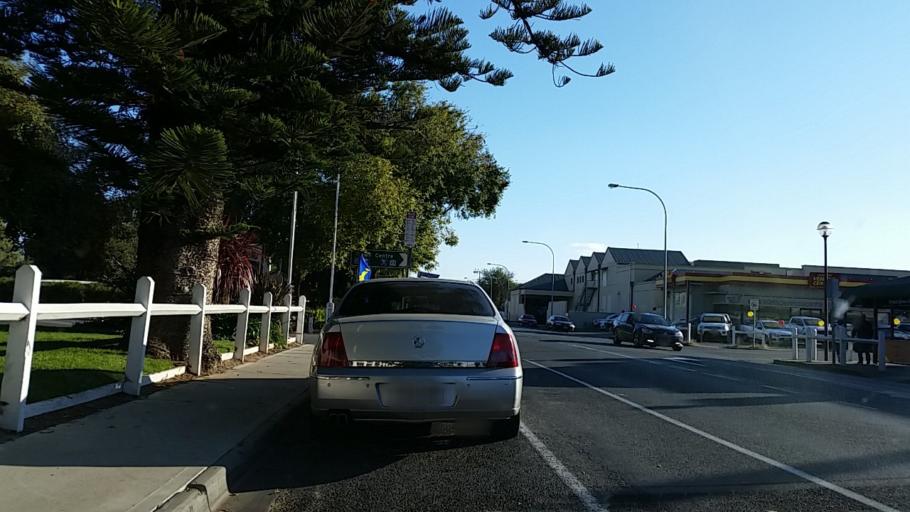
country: AU
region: South Australia
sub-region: Alexandrina
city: Strathalbyn
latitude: -35.2608
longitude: 138.8920
